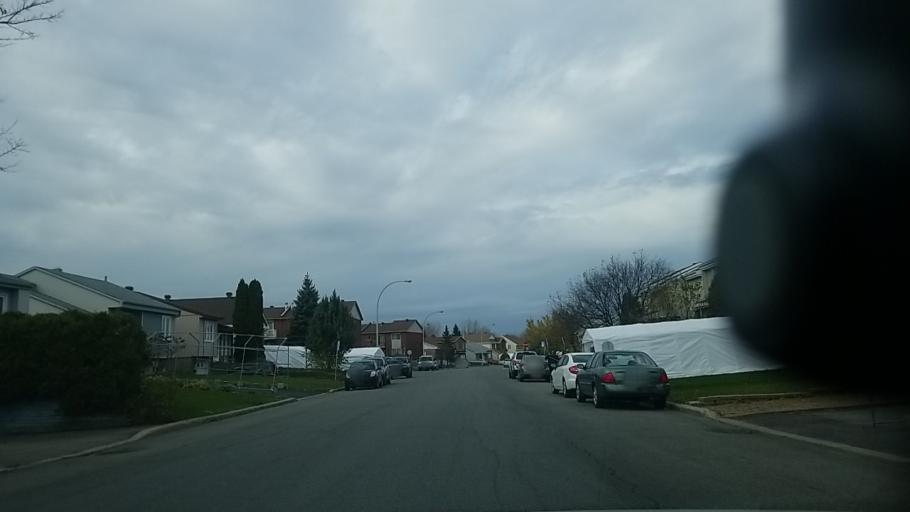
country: CA
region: Quebec
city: Dollard-Des Ormeaux
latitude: 45.5379
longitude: -73.7867
